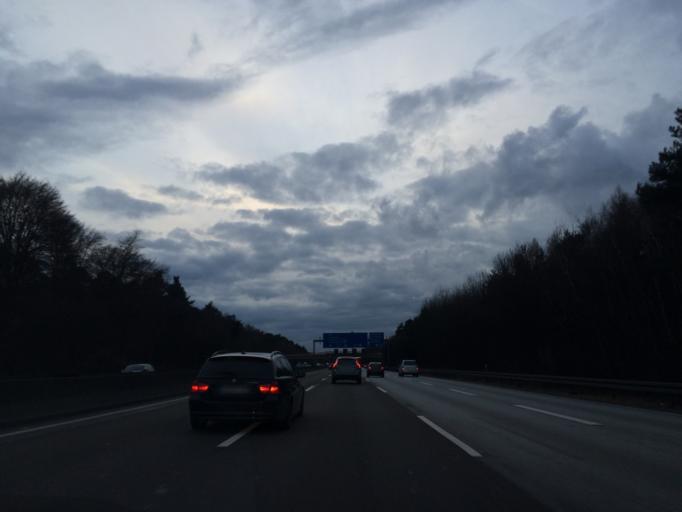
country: DE
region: Hesse
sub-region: Regierungsbezirk Darmstadt
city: Offenbach
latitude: 50.0661
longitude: 8.7582
